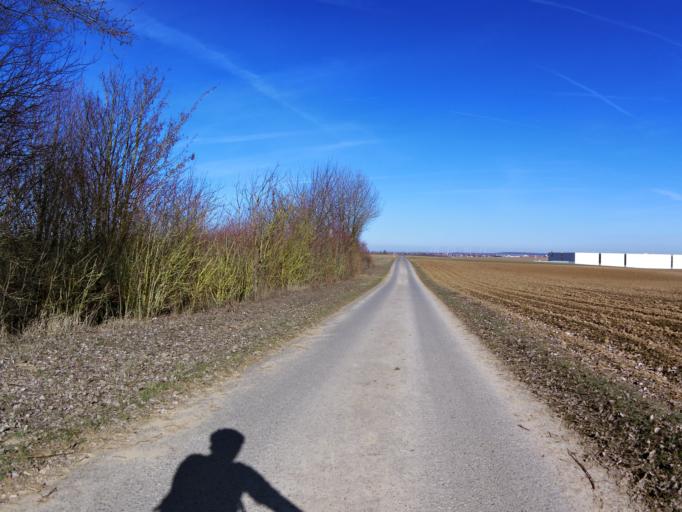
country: DE
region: Bavaria
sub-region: Regierungsbezirk Unterfranken
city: Kurnach
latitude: 49.8502
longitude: 10.0188
